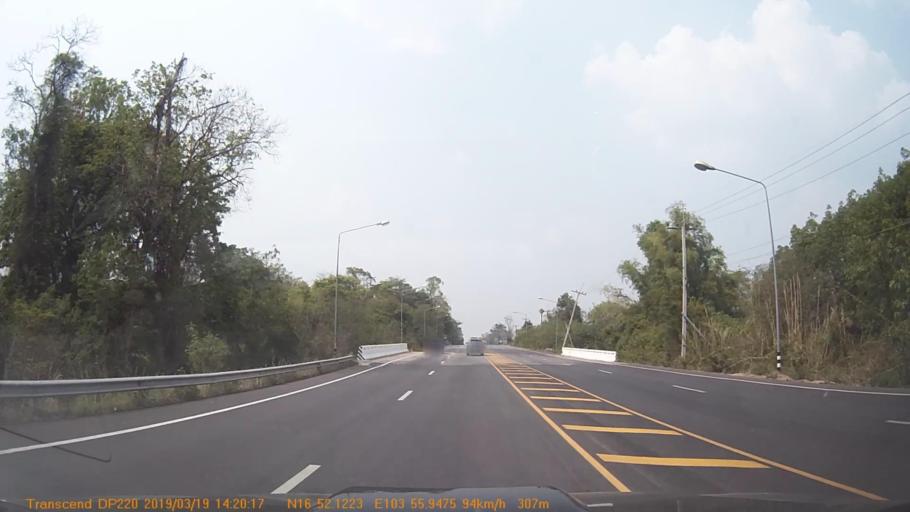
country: TH
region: Sakon Nakhon
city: Phu Phan
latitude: 16.8693
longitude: 103.9324
